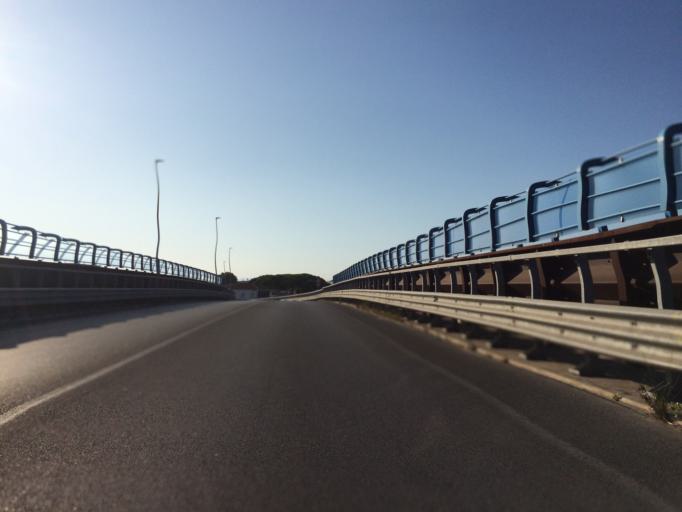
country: IT
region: Tuscany
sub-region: Provincia di Lucca
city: Viareggio
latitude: 43.8618
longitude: 10.2614
